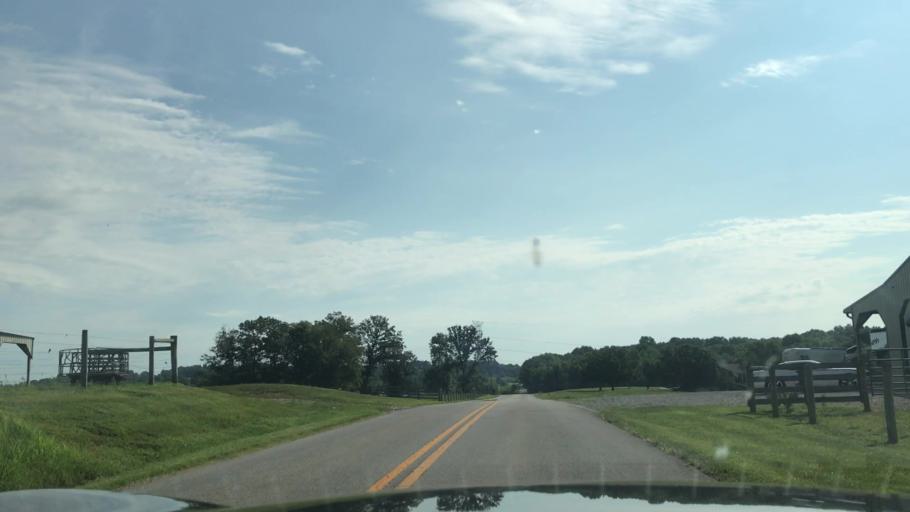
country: US
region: Kentucky
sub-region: Hart County
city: Munfordville
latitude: 37.2274
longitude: -85.7172
